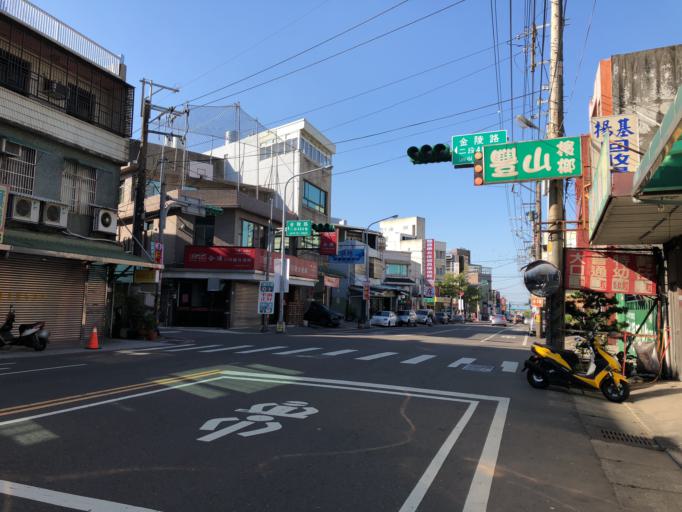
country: TW
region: Taiwan
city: Daxi
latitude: 24.9327
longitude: 121.2257
